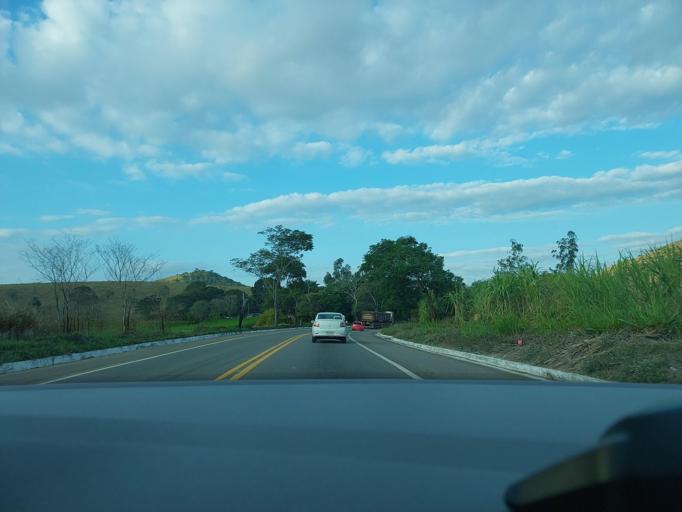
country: BR
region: Minas Gerais
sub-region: Muriae
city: Muriae
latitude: -21.1246
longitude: -42.2706
